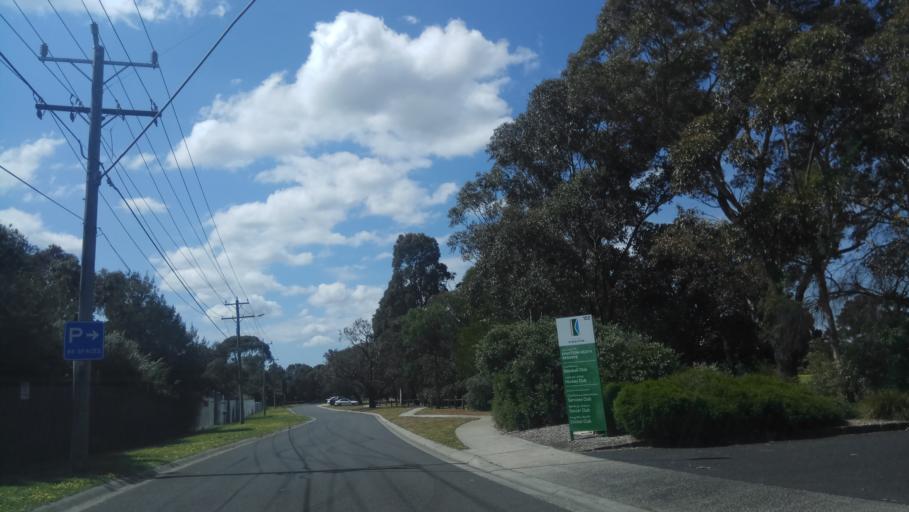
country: AU
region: Victoria
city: Heatherton
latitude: -37.9641
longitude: 145.0878
